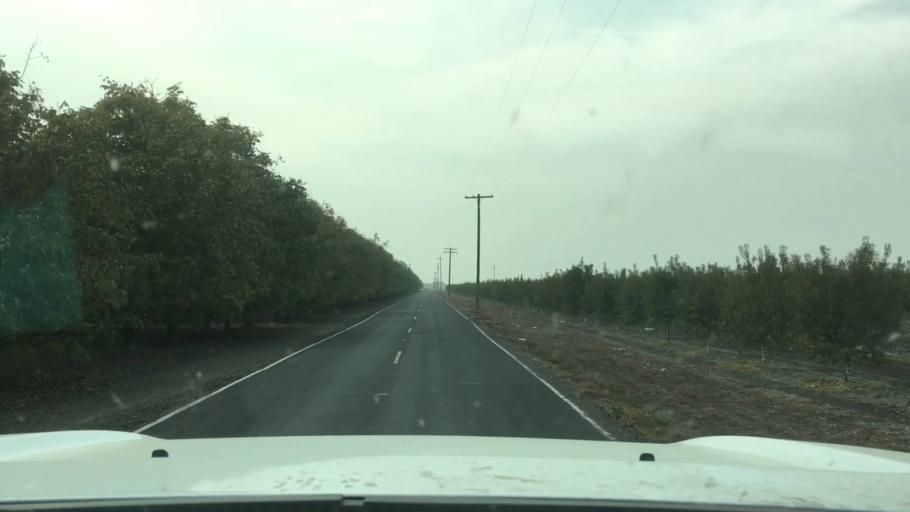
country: US
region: California
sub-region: San Joaquin County
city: Manteca
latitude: 37.8631
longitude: -121.1371
